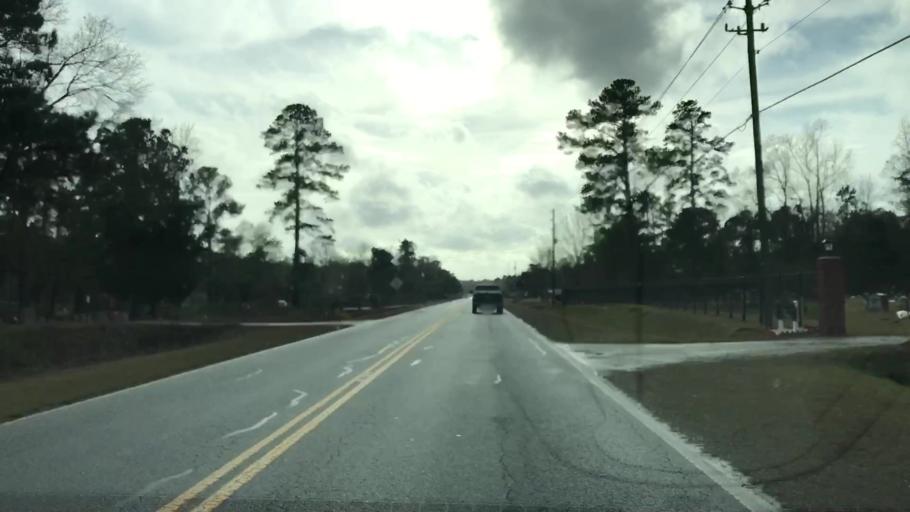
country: US
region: South Carolina
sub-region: Williamsburg County
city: Andrews
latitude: 33.4498
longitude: -79.5839
